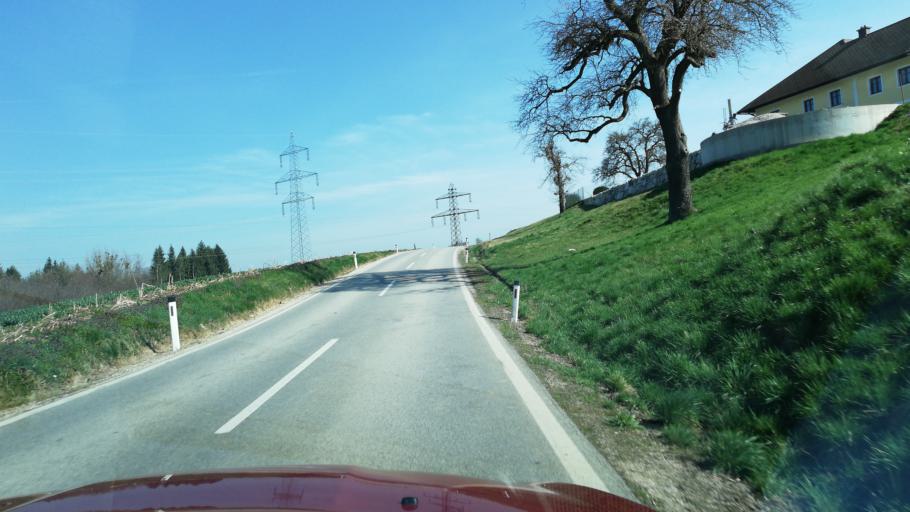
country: AT
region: Upper Austria
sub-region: Politischer Bezirk Kirchdorf an der Krems
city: Kremsmunster
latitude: 48.0898
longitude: 14.1097
